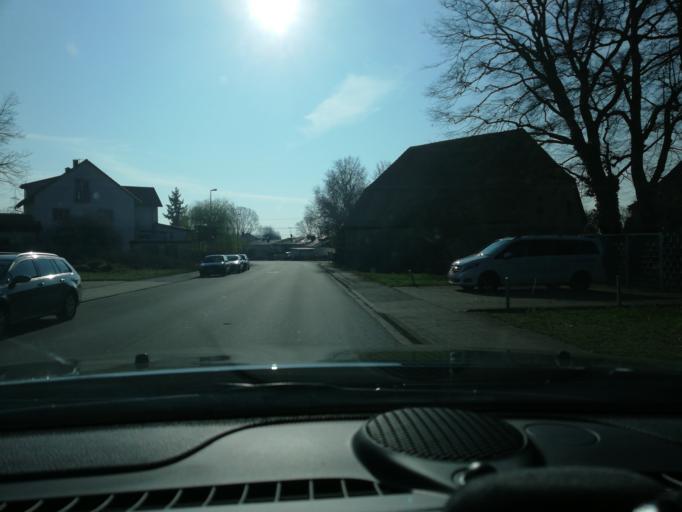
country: DE
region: Bavaria
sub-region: Regierungsbezirk Mittelfranken
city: Hessdorf
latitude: 49.6011
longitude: 10.9374
